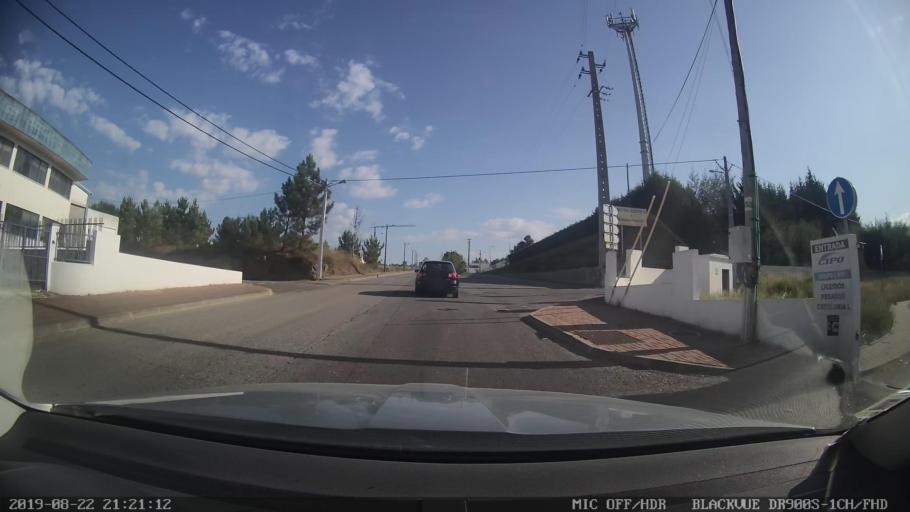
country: PT
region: Castelo Branco
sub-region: Serta
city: Serta
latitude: 39.8170
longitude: -8.1088
